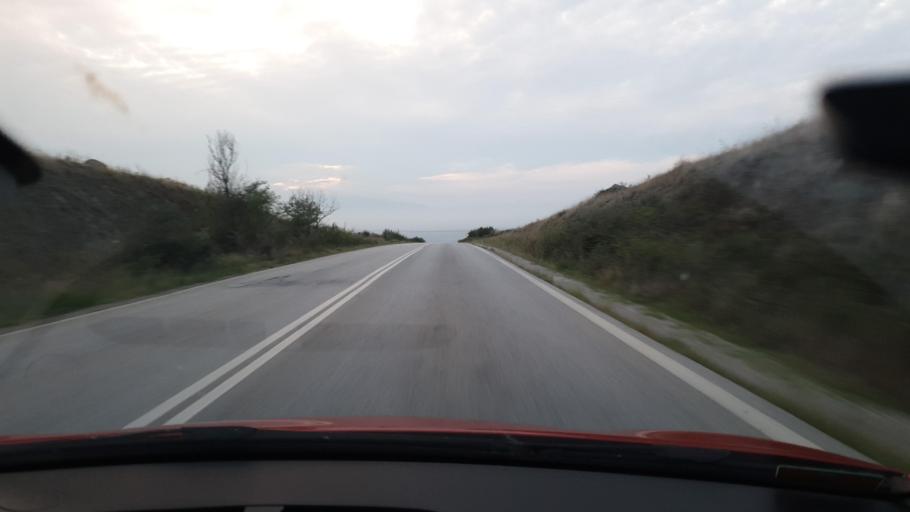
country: GR
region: Central Macedonia
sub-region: Nomos Kilkis
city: Polykastro
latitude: 41.0050
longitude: 22.7120
